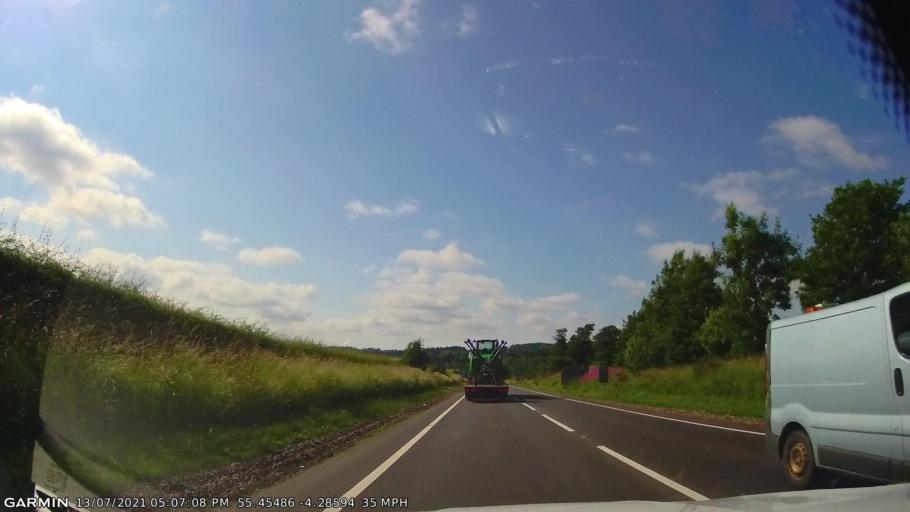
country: GB
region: Scotland
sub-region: East Ayrshire
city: Auchinleck
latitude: 55.4549
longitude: -4.2863
